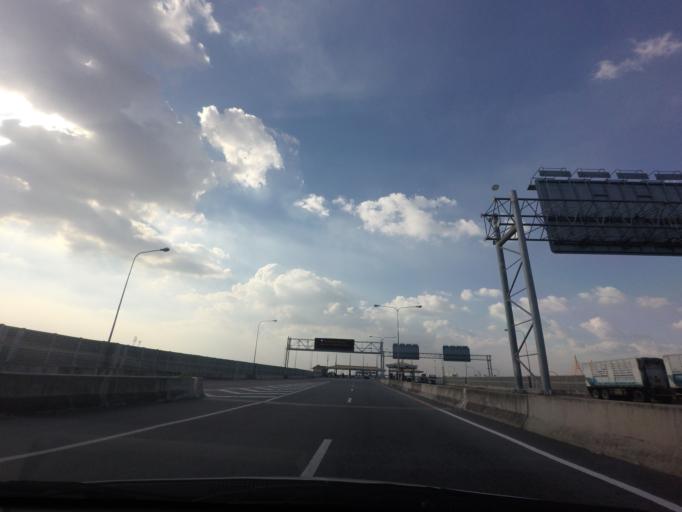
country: TH
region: Samut Prakan
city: Phra Pradaeng
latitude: 13.6422
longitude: 100.5482
